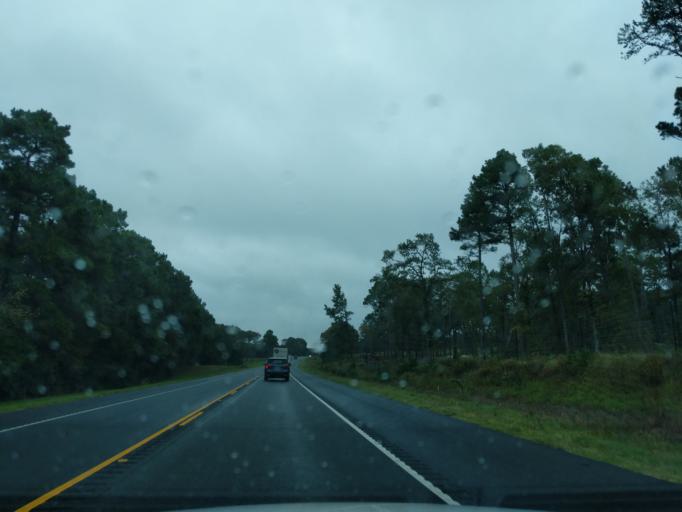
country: US
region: Louisiana
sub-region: Caddo Parish
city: Greenwood
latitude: 32.4324
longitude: -93.9844
